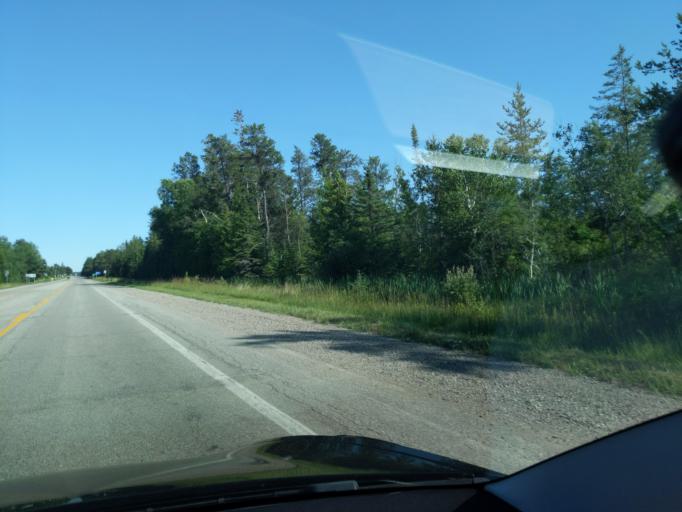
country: US
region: Michigan
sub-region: Mackinac County
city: Saint Ignace
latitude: 45.7636
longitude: -84.7166
